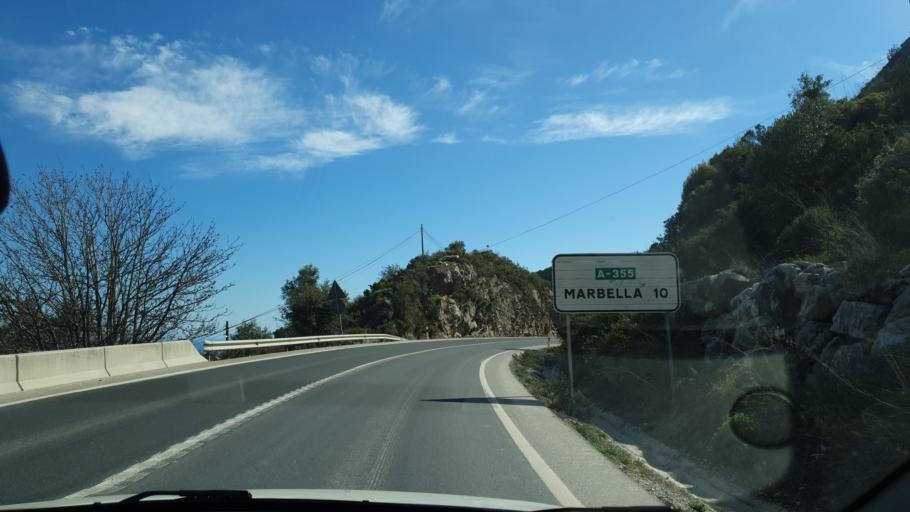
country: ES
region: Andalusia
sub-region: Provincia de Malaga
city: Ojen
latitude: 36.5819
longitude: -4.8527
